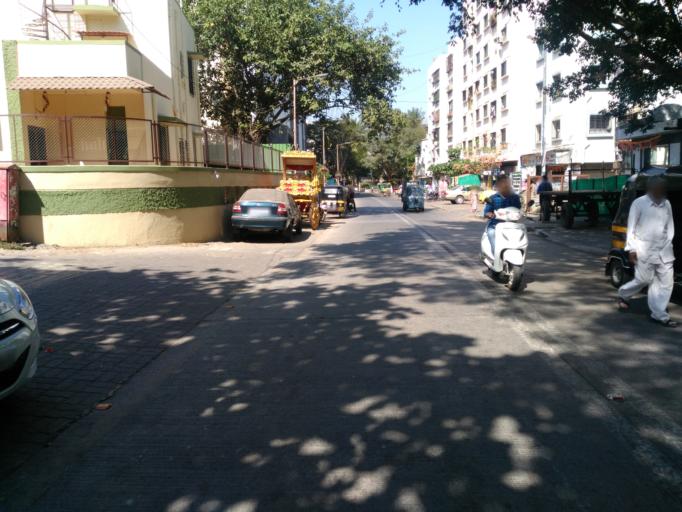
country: IN
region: Maharashtra
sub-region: Pune Division
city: Pune
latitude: 18.4844
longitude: 73.8517
